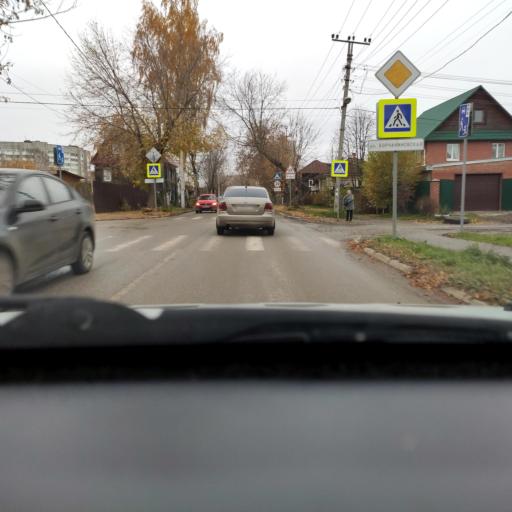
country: RU
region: Perm
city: Perm
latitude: 58.0267
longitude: 56.3321
